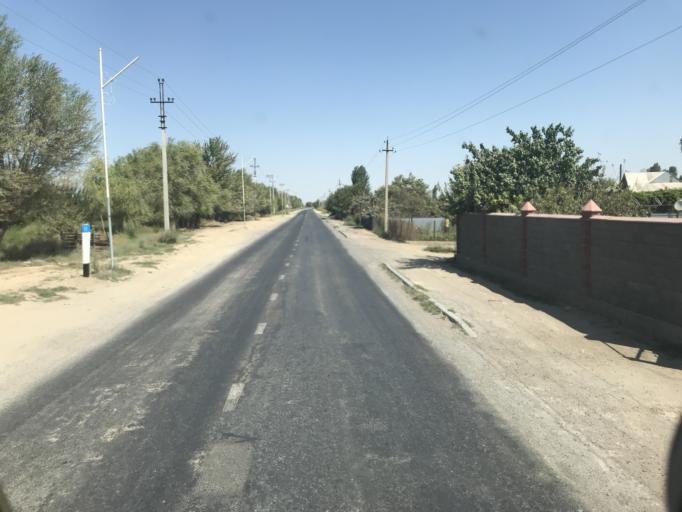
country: KZ
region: Ongtustik Qazaqstan
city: Ilyich
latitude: 40.9393
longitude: 68.4883
